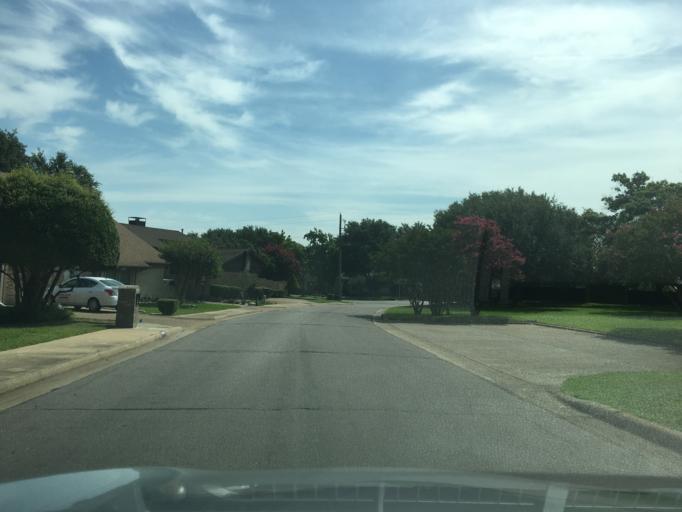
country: US
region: Texas
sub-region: Dallas County
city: Addison
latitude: 32.9257
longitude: -96.7990
